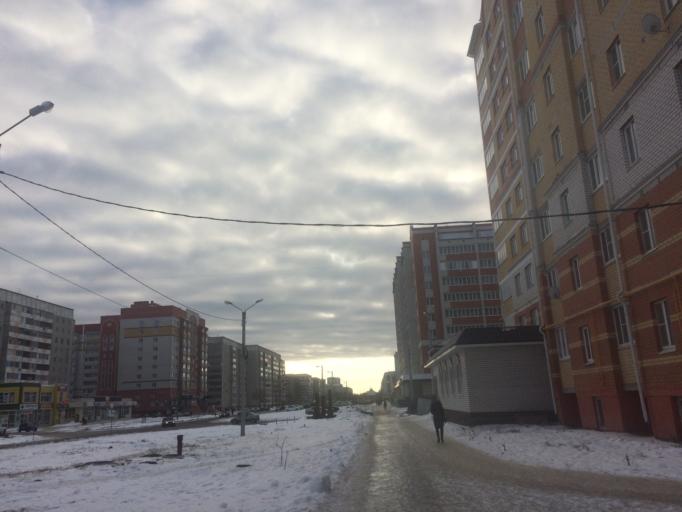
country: RU
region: Mariy-El
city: Yoshkar-Ola
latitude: 56.6403
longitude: 47.9240
